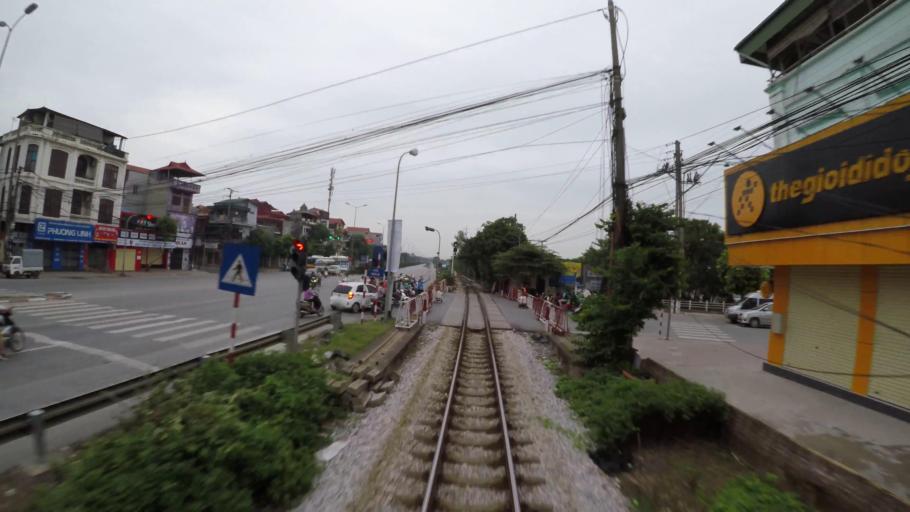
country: VN
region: Hung Yen
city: Nhu Quynh
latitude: 21.0018
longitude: 105.9646
